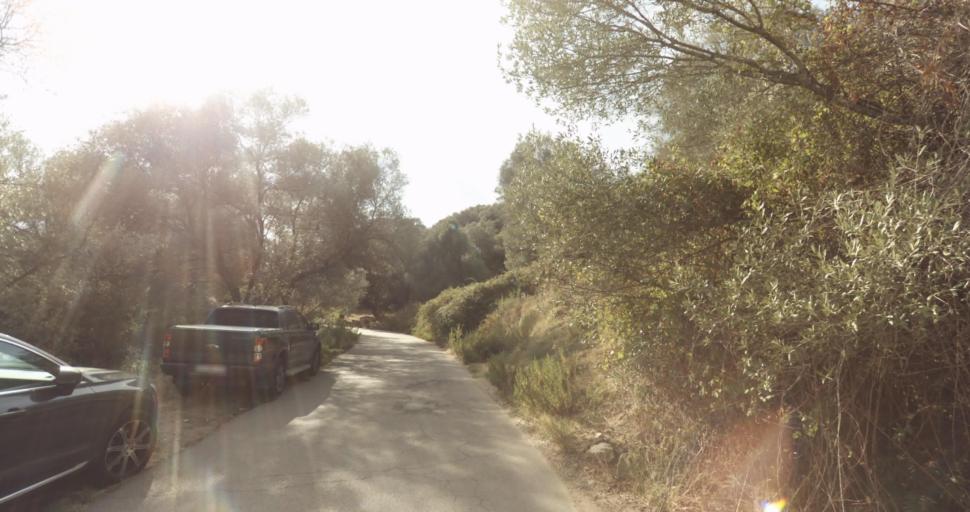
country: FR
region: Corsica
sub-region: Departement de la Corse-du-Sud
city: Ajaccio
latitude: 41.9351
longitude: 8.7197
